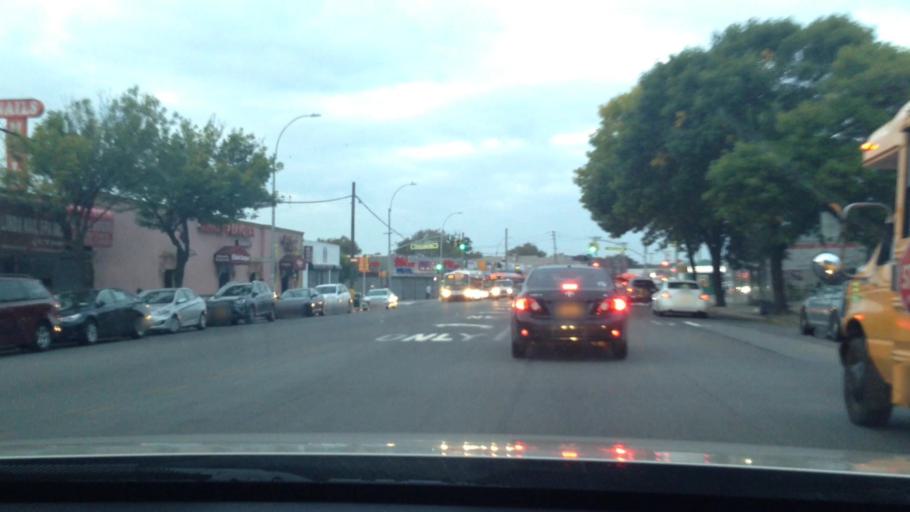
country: US
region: New York
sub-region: Nassau County
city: Bellerose Terrace
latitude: 40.7216
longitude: -73.7587
